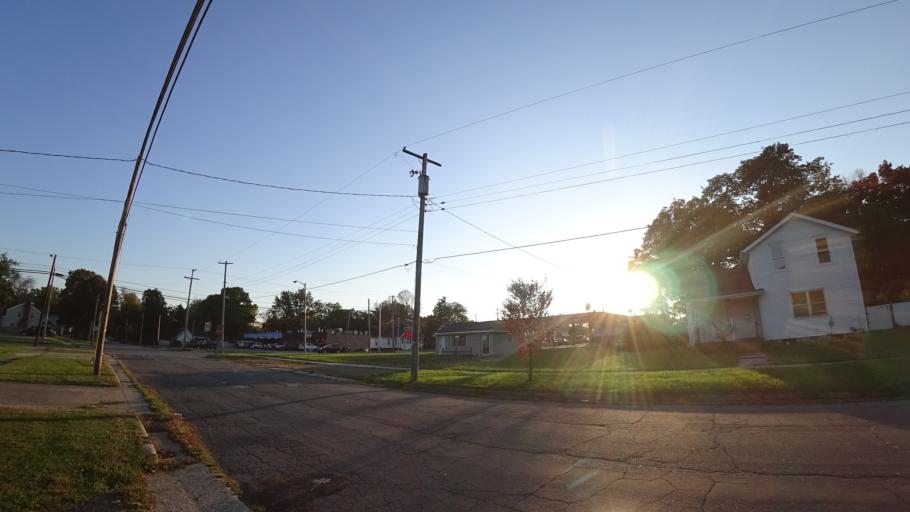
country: US
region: Michigan
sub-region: Saint Joseph County
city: Three Rivers
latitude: 41.9431
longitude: -85.6406
